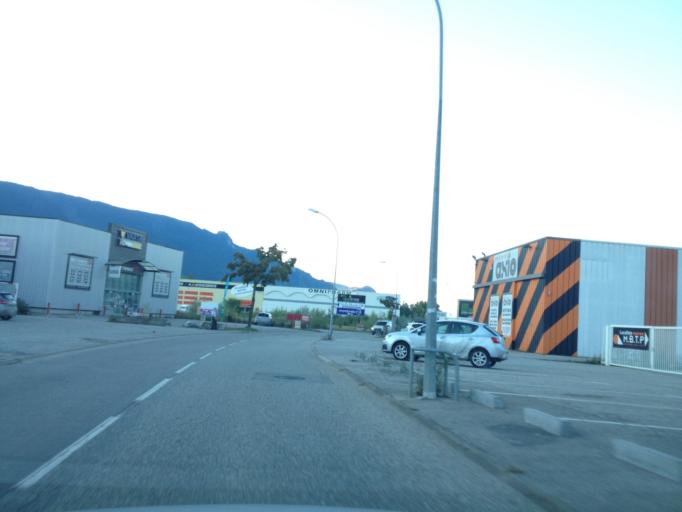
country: FR
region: Rhone-Alpes
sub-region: Departement de la Savoie
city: La Motte-Servolex
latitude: 45.6043
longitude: 5.8924
